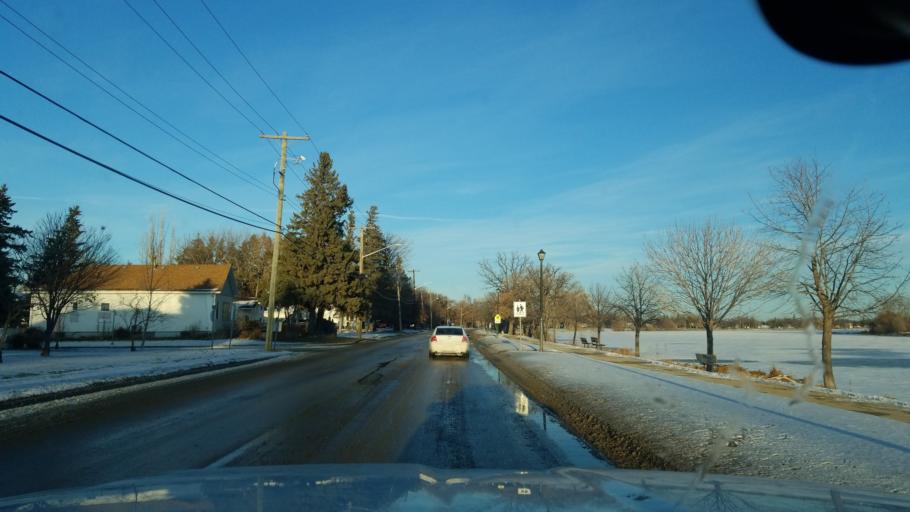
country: CA
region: Manitoba
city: Portage la Prairie
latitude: 49.9666
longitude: -98.3185
